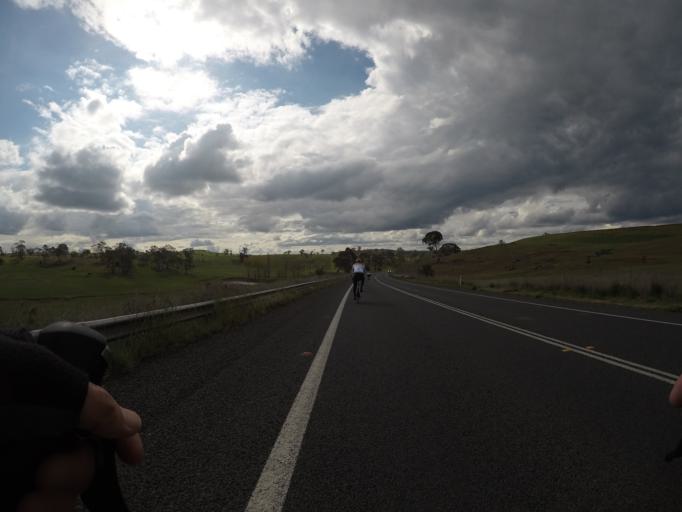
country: AU
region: New South Wales
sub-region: Blayney
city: Millthorpe
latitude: -33.4114
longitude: 149.2447
